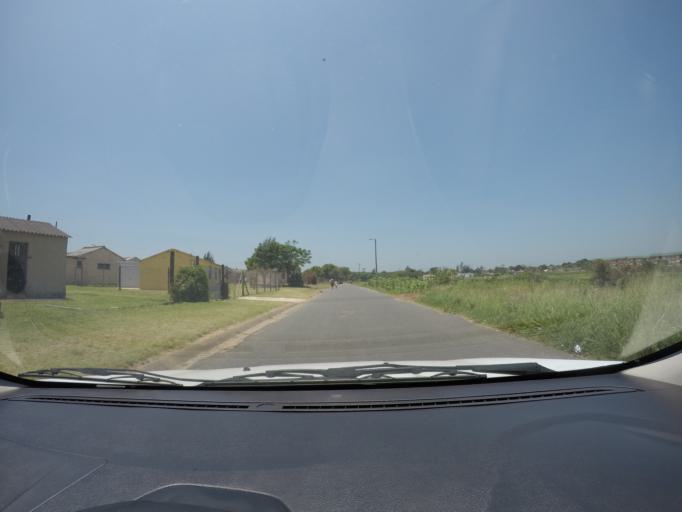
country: ZA
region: KwaZulu-Natal
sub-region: uThungulu District Municipality
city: eSikhawini
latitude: -28.8790
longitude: 31.9052
